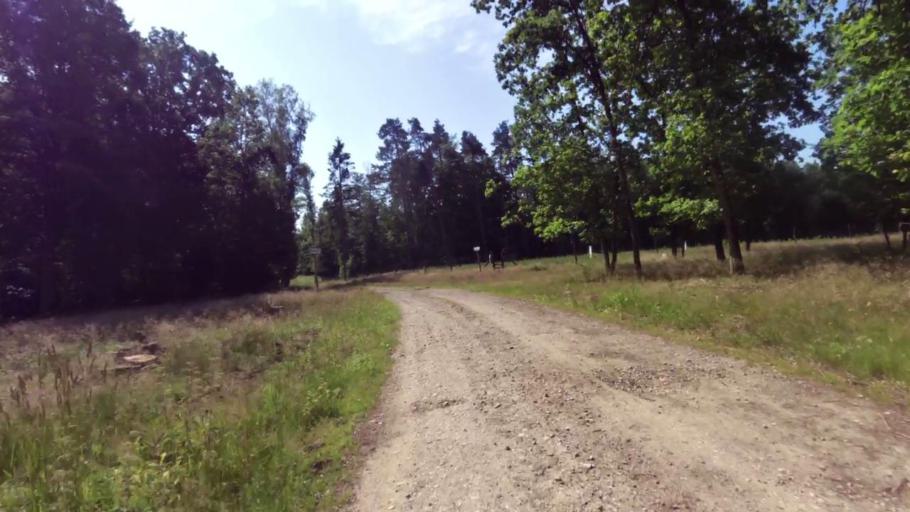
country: PL
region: West Pomeranian Voivodeship
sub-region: Powiat swidwinski
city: Polczyn-Zdroj
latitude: 53.8510
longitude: 16.1405
